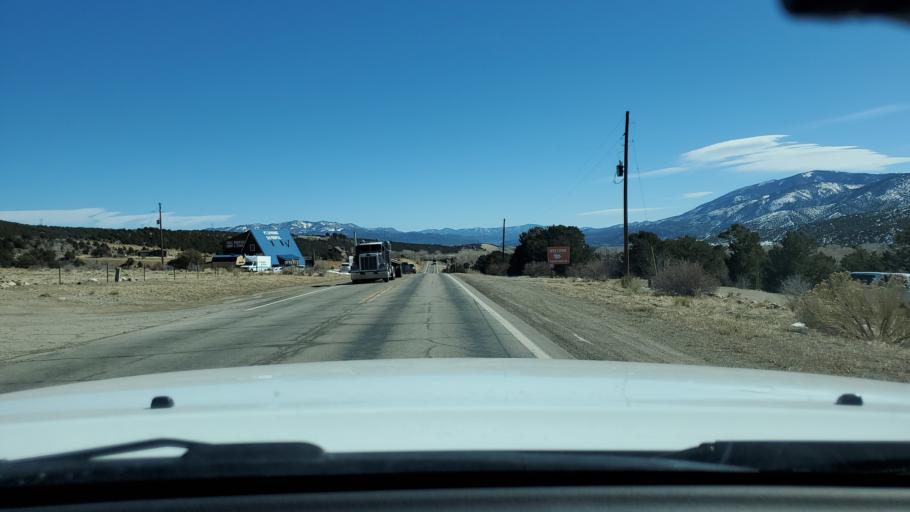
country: US
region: Colorado
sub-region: Chaffee County
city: Salida
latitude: 38.5360
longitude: -106.1758
